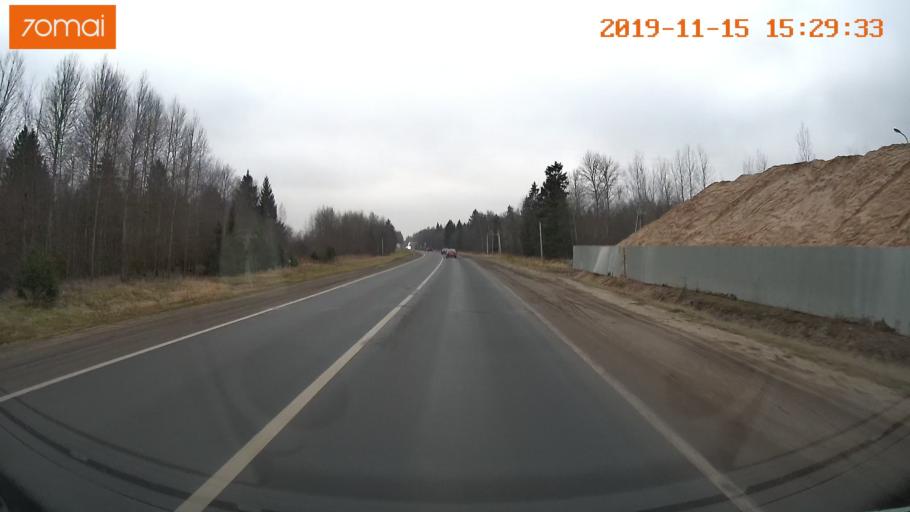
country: RU
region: Jaroslavl
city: Danilov
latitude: 58.1196
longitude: 40.1189
